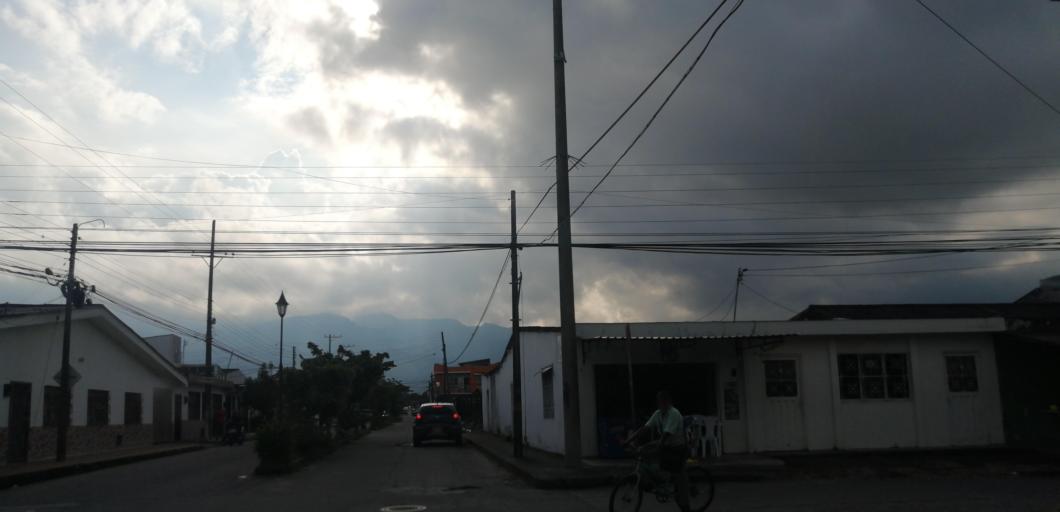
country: CO
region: Meta
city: Acacias
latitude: 3.9856
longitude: -73.7680
